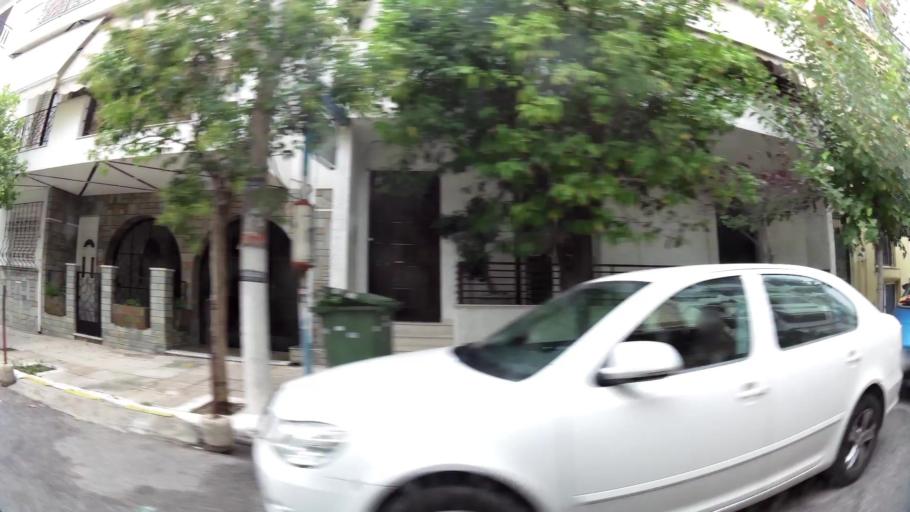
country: GR
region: Attica
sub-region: Nomos Piraios
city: Korydallos
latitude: 37.9835
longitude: 23.6437
